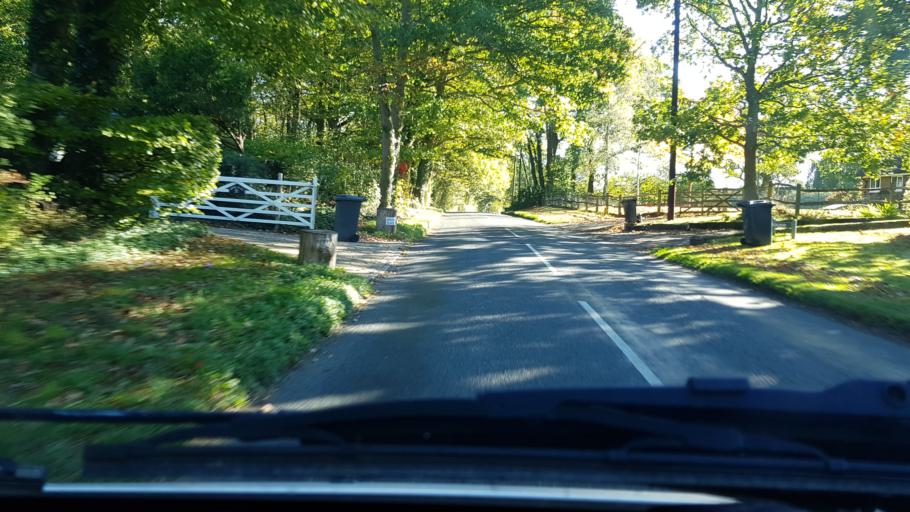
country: GB
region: England
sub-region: West Sussex
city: Rudgwick
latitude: 51.1338
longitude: -0.4207
